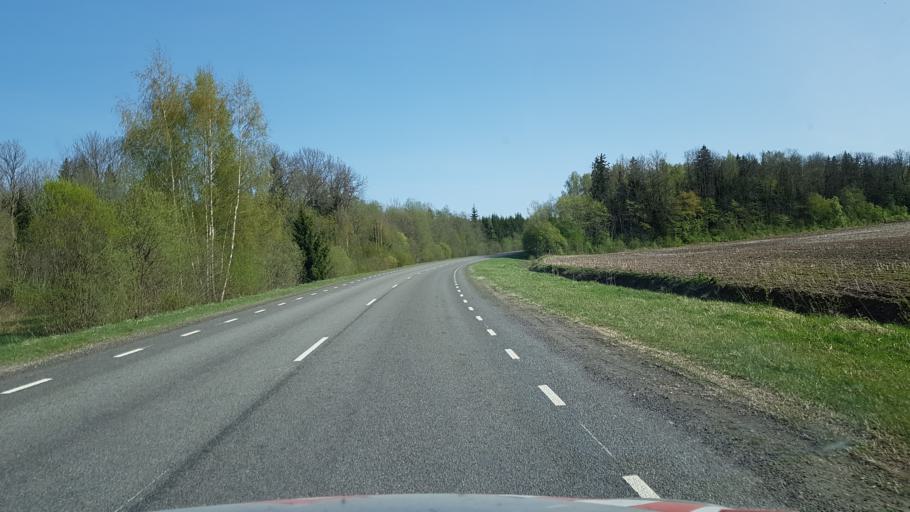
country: EE
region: Viljandimaa
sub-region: Karksi vald
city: Karksi-Nuia
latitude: 58.2065
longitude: 25.5372
